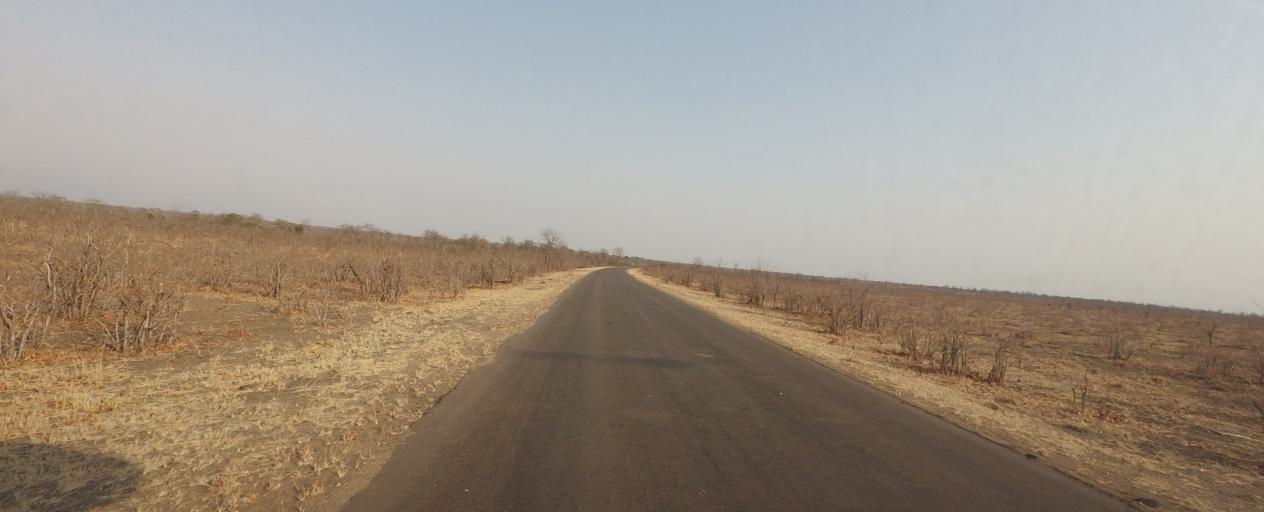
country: ZA
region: Limpopo
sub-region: Mopani District Municipality
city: Giyani
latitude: -23.0749
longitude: 31.4094
